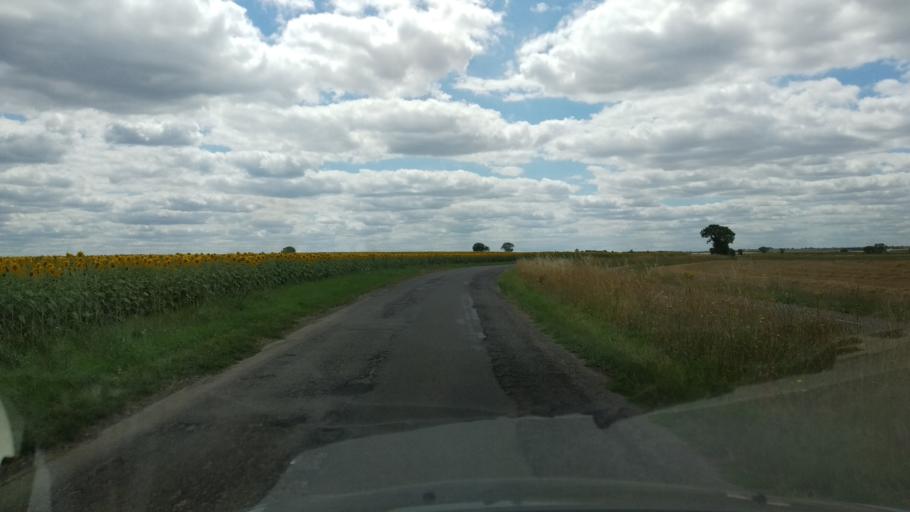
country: FR
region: Poitou-Charentes
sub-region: Departement de la Vienne
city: Avanton
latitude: 46.6742
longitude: 0.3368
